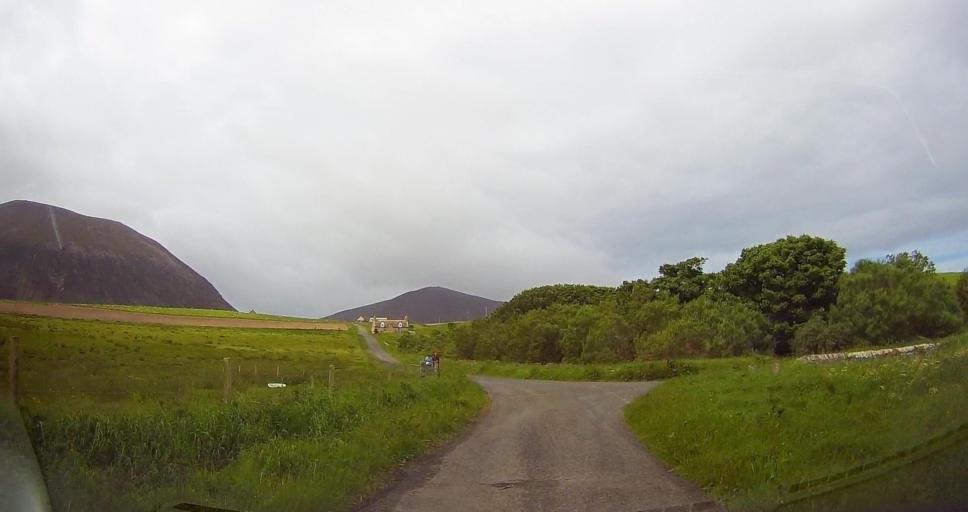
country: GB
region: Scotland
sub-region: Orkney Islands
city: Stromness
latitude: 58.9164
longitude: -3.3230
